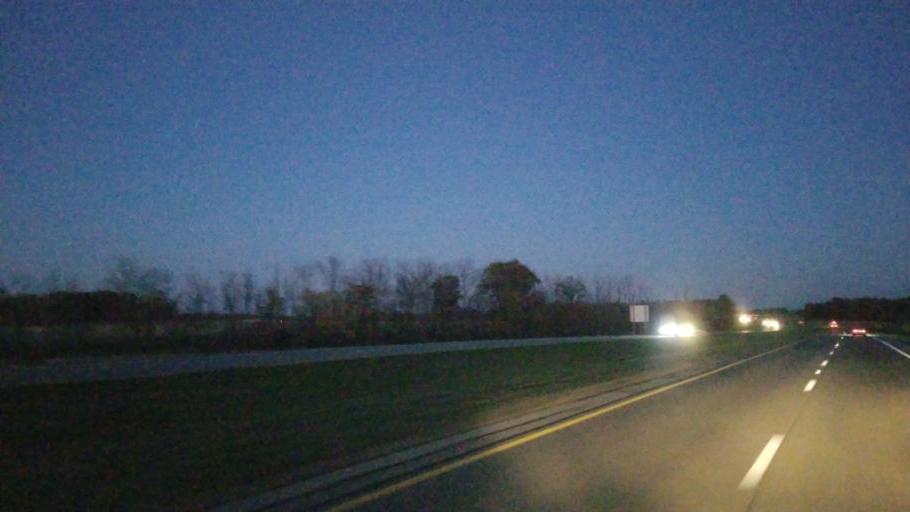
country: US
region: Ohio
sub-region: Crawford County
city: Crestline
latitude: 40.7622
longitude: -82.7222
